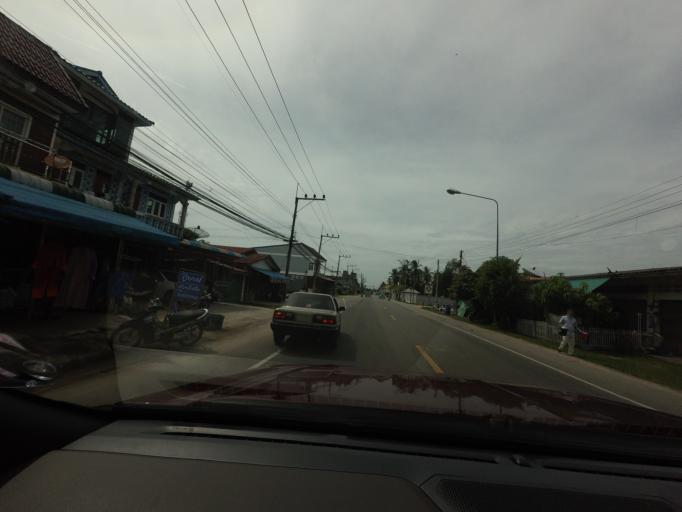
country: TH
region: Narathiwat
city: Tak Bai
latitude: 6.2396
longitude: 102.0813
